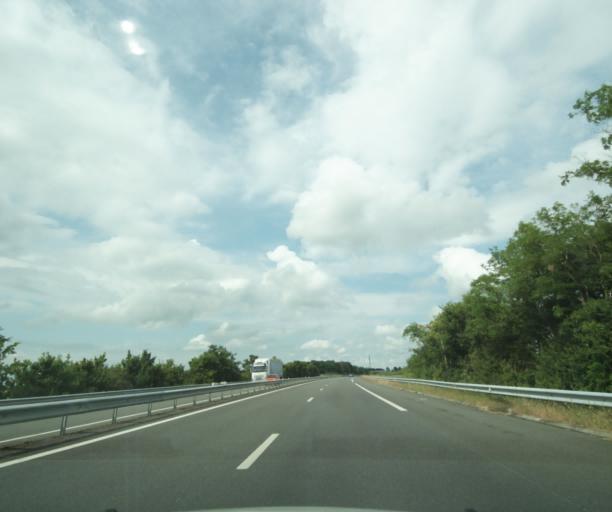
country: FR
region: Centre
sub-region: Departement du Cher
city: Levet
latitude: 46.8424
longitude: 2.4166
